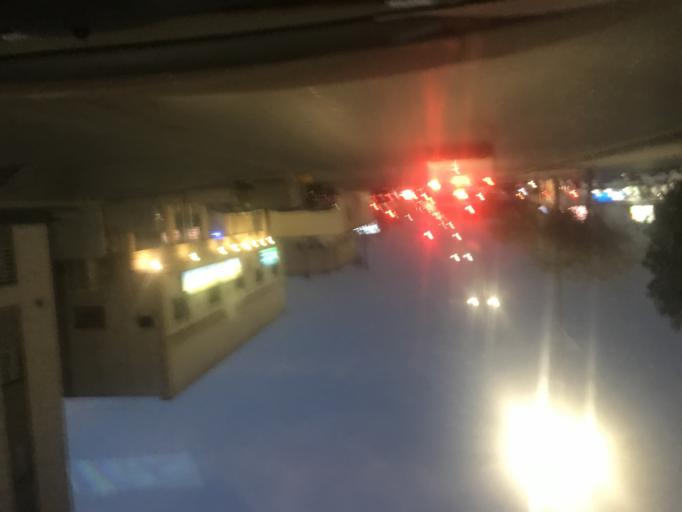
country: SA
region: Ar Riyad
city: Riyadh
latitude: 24.7319
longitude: 46.7615
